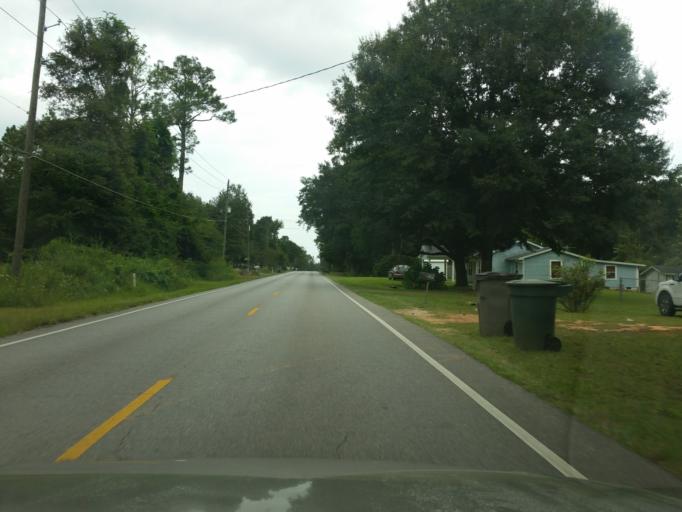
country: US
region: Florida
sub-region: Escambia County
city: Molino
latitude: 30.6854
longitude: -87.3246
